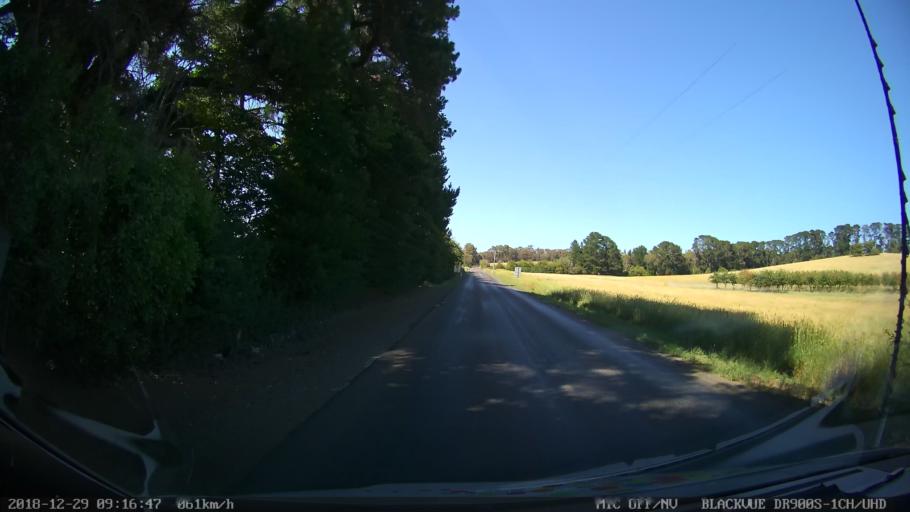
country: AU
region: New South Wales
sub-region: Upper Lachlan Shire
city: Crookwell
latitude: -34.4612
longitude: 149.4494
